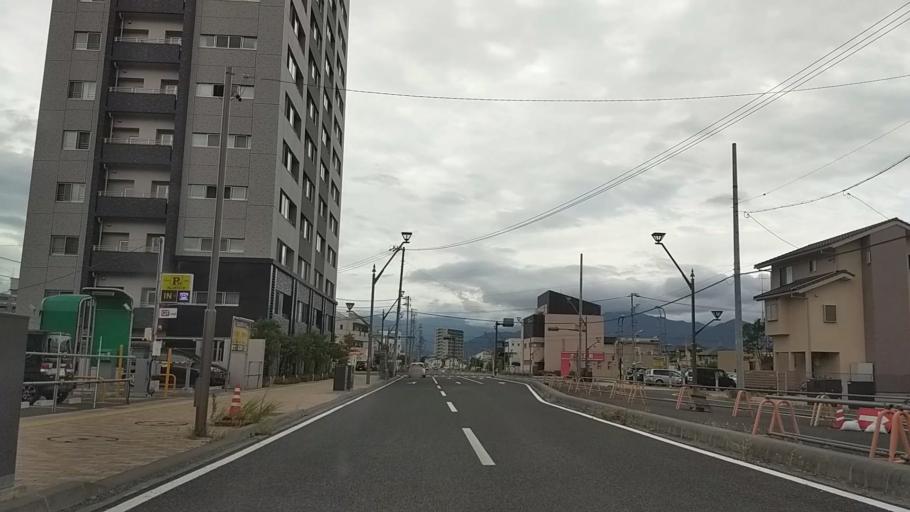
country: JP
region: Nagano
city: Nagano-shi
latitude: 36.6401
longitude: 138.1865
